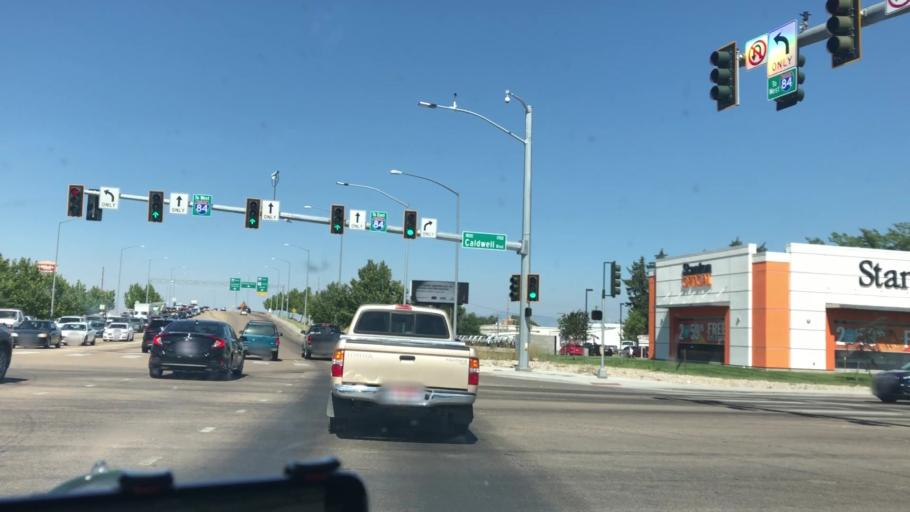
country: US
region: Idaho
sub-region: Canyon County
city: Nampa
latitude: 43.6053
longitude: -116.6030
